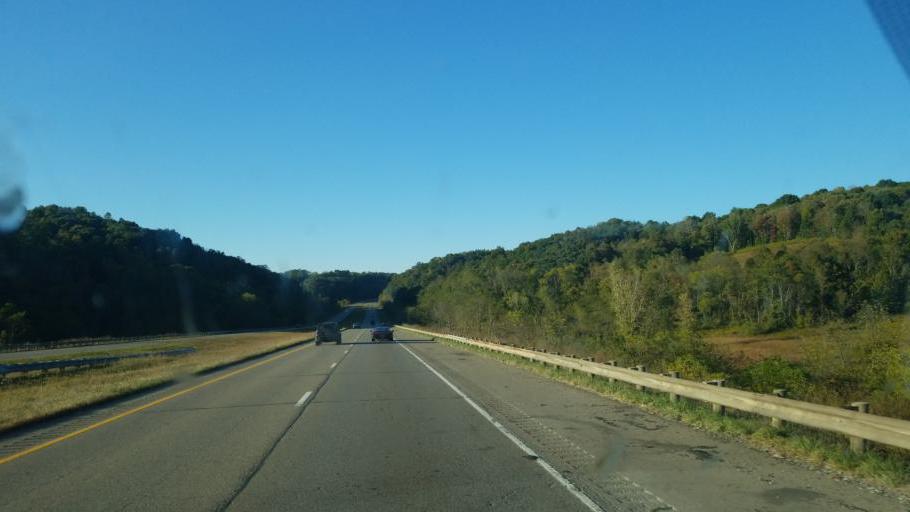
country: US
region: Ohio
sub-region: Tuscarawas County
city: Newcomerstown
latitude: 40.1807
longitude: -81.5542
